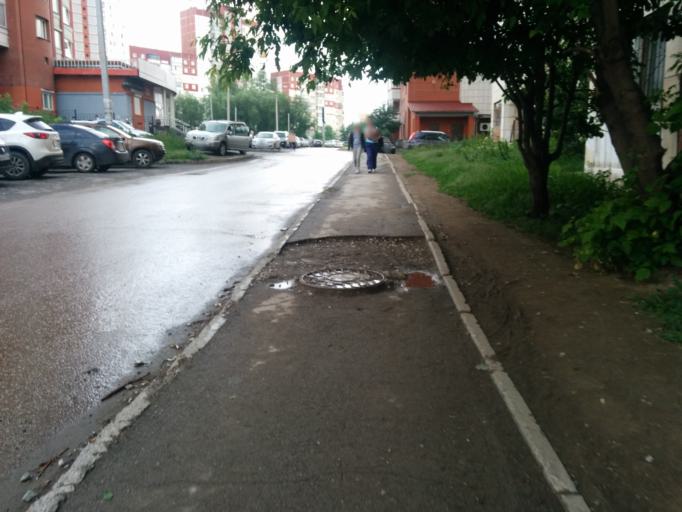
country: RU
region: Perm
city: Perm
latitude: 58.0085
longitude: 56.3014
